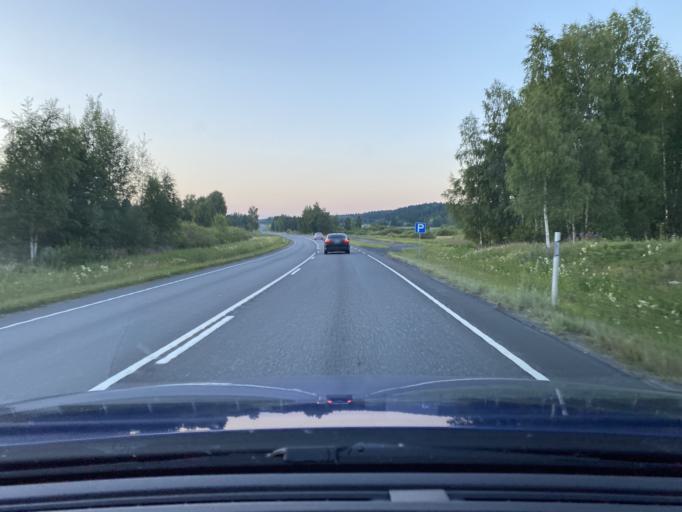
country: FI
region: Pirkanmaa
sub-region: Luoteis-Pirkanmaa
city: Ikaalinen
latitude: 61.8649
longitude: 22.9607
